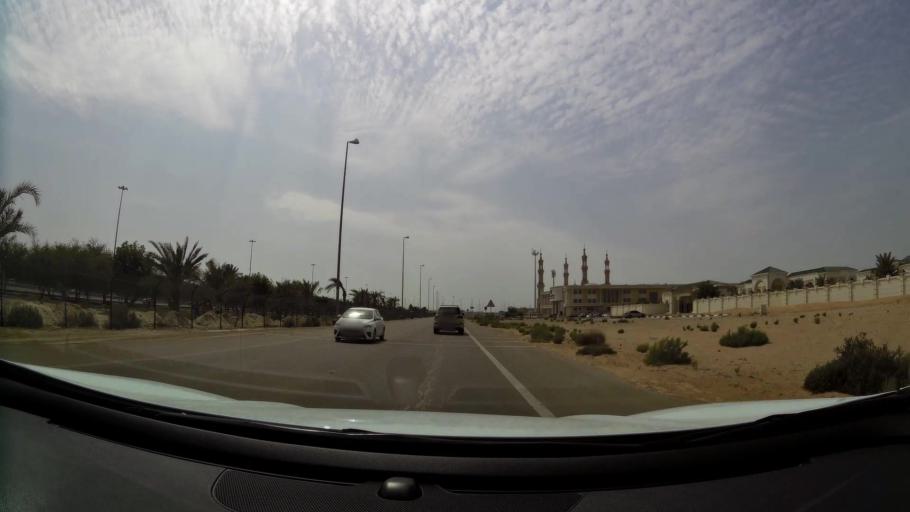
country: AE
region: Abu Dhabi
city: Abu Dhabi
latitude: 24.5180
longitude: 54.6682
